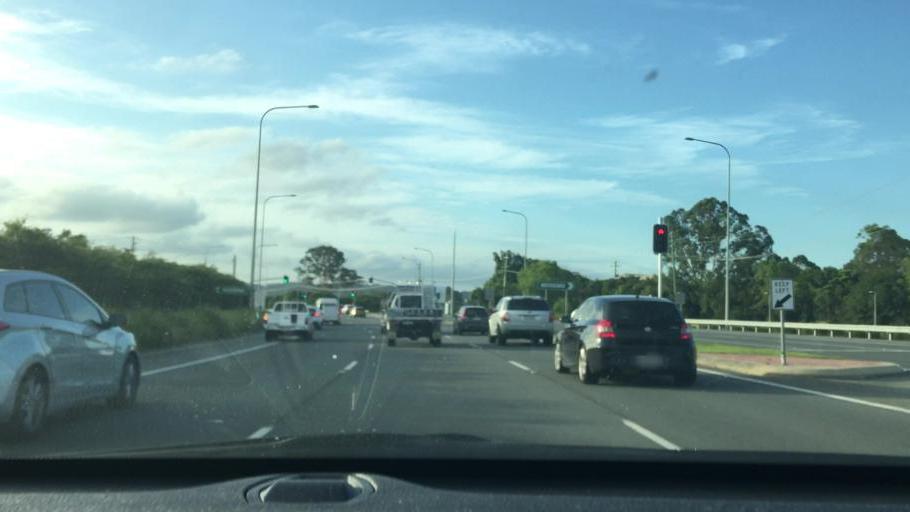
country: AU
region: Queensland
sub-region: Gold Coast
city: Nerang
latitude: -28.0019
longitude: 153.3611
